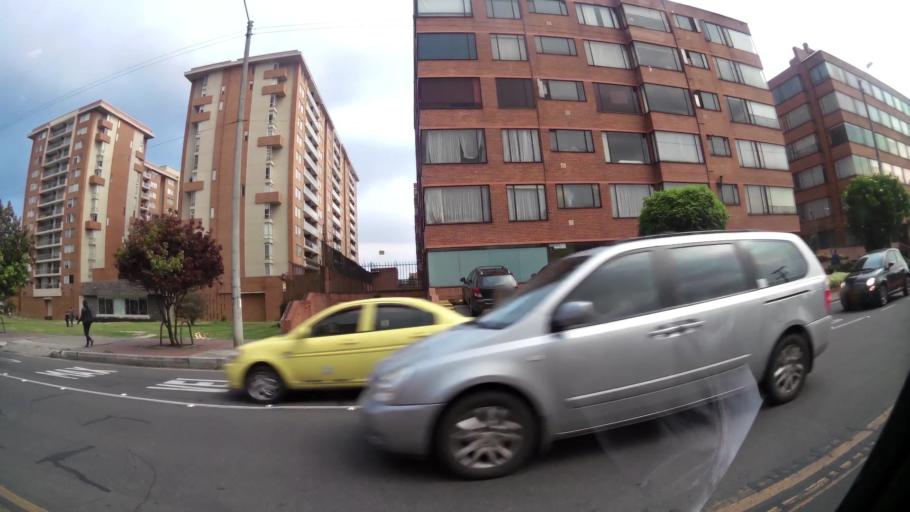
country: CO
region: Bogota D.C.
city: Barrio San Luis
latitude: 4.7288
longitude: -74.0661
